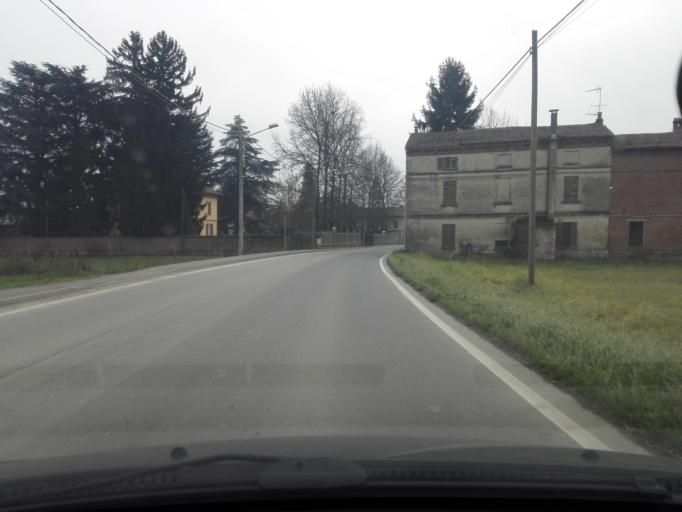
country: IT
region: Piedmont
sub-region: Provincia di Alessandria
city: Casal Cermelli
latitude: 44.8396
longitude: 8.6225
